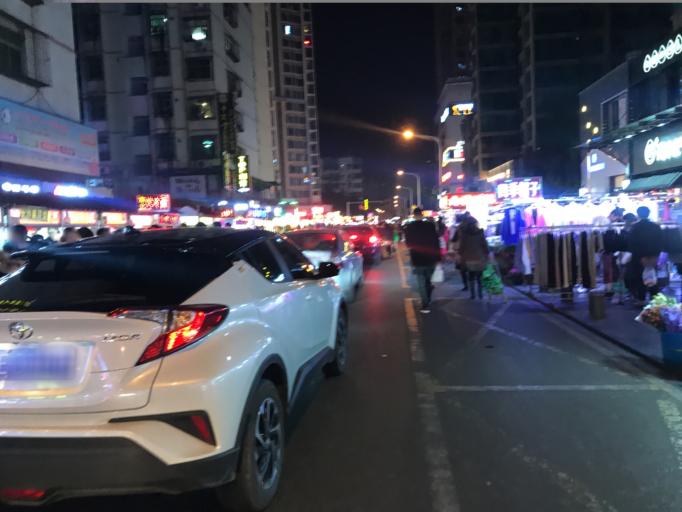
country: CN
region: Hubei
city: Yichang
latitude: 30.7080
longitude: 111.2844
